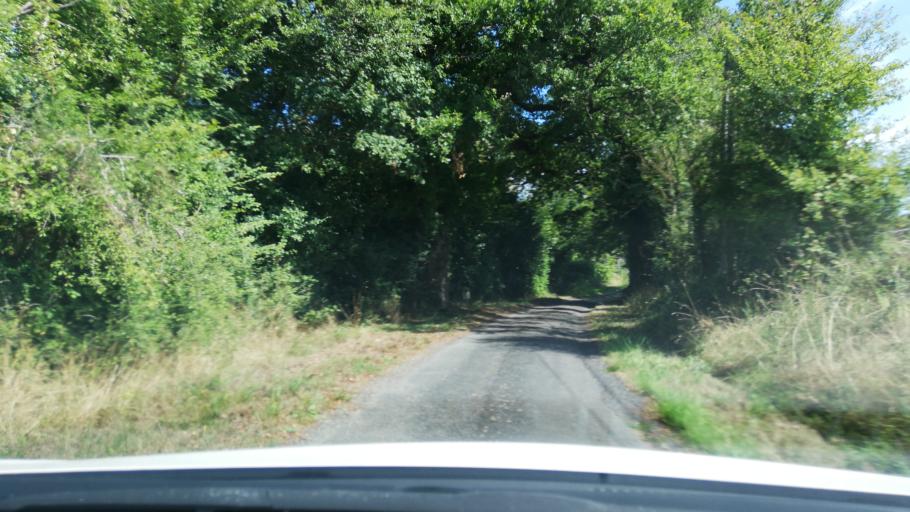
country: FR
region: Centre
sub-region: Departement d'Indre-et-Loire
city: Mazieres-de-Touraine
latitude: 47.3977
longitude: 0.4447
